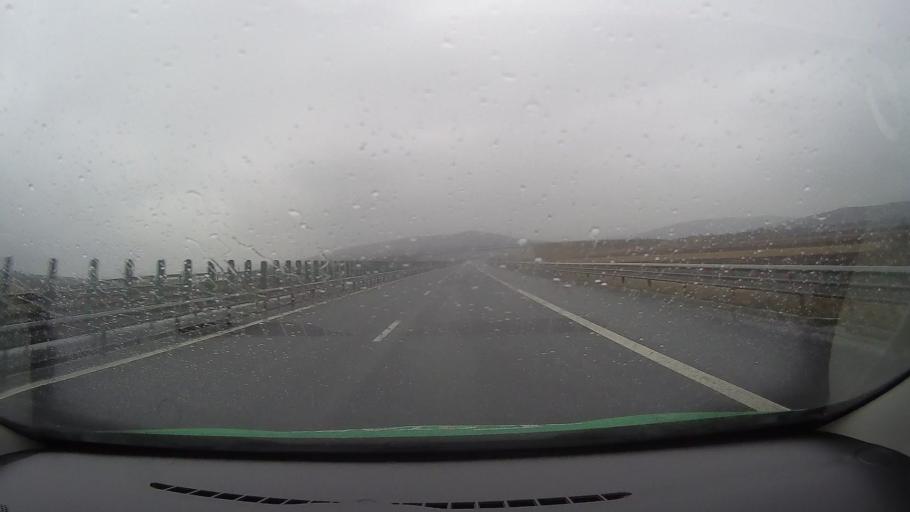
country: RO
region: Sibiu
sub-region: Comuna Apoldu de Jos
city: Apoldu de Jos
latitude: 45.8901
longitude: 23.8375
